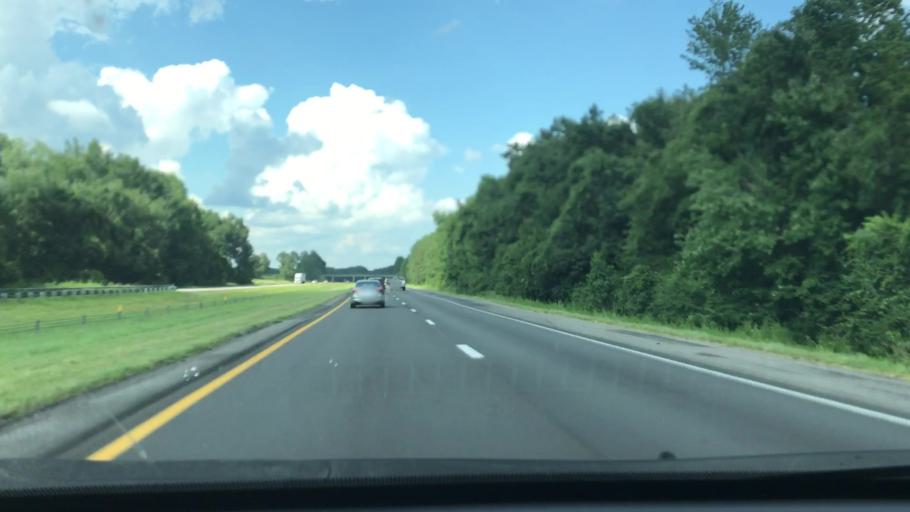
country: US
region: South Carolina
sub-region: Clarendon County
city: Manning
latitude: 33.8131
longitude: -80.1510
